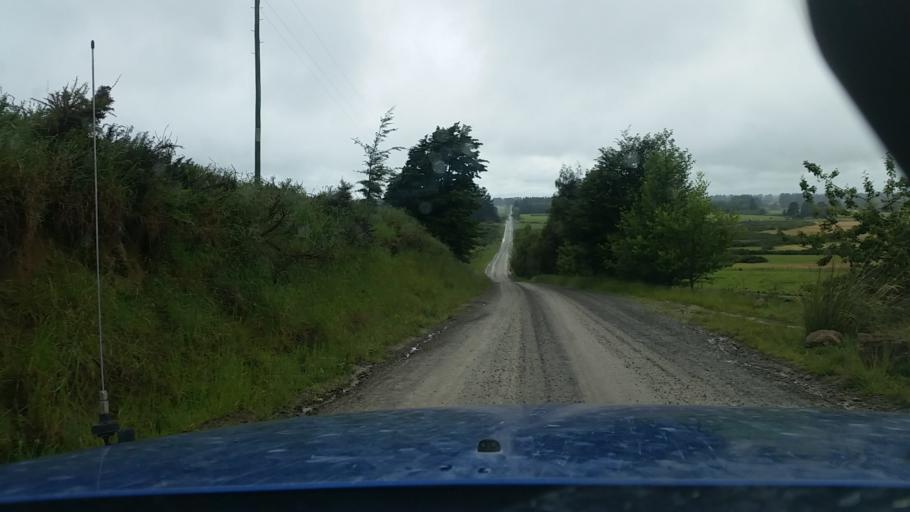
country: NZ
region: Canterbury
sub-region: Ashburton District
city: Methven
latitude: -43.6058
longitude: 171.4658
